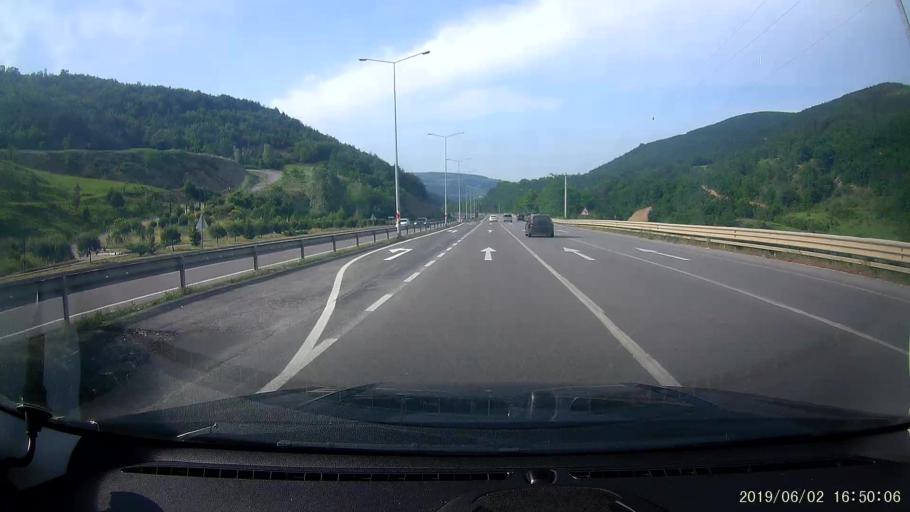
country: TR
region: Samsun
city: Samsun
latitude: 41.2476
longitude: 36.1729
